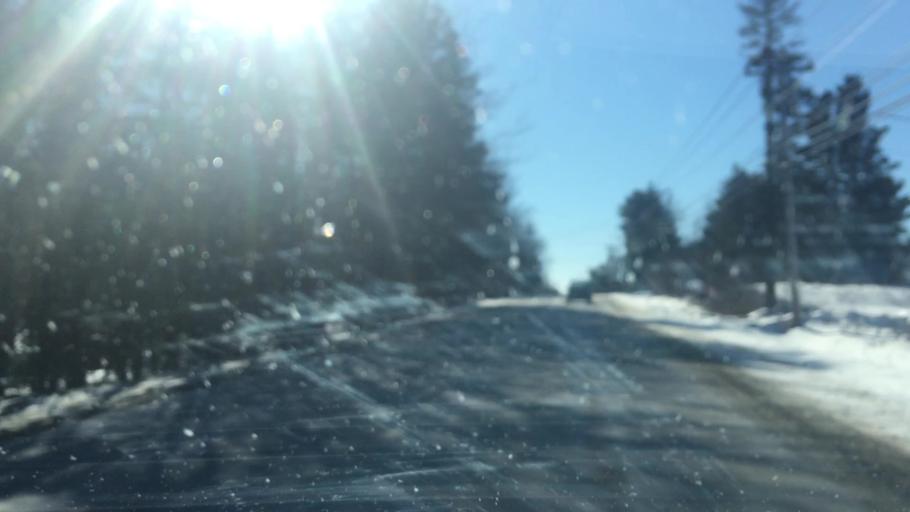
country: US
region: Maine
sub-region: Hancock County
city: Ellsworth
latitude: 44.5181
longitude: -68.4323
